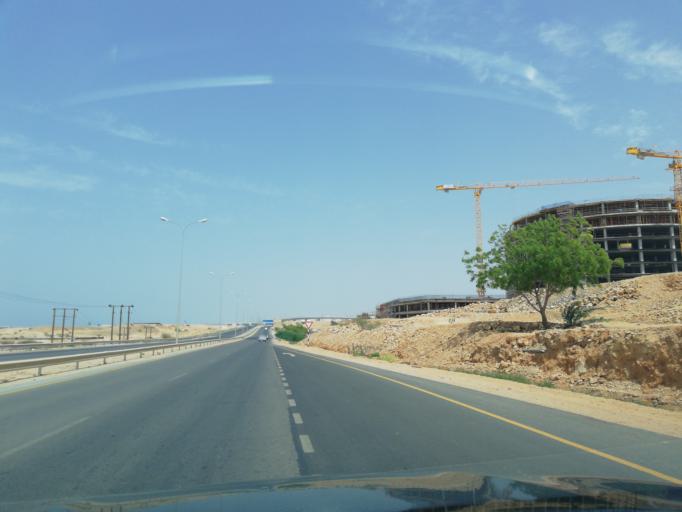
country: OM
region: Muhafazat Masqat
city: Bawshar
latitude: 23.5813
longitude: 58.3229
